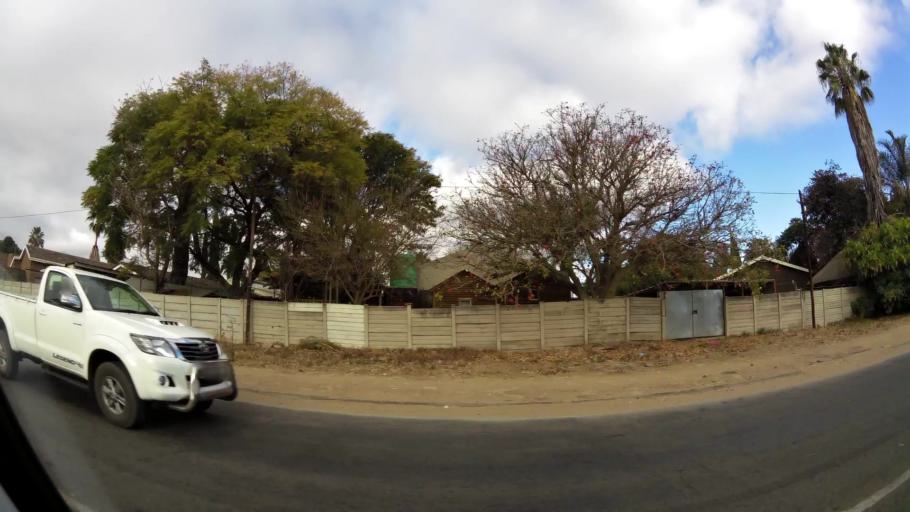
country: ZA
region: Limpopo
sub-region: Capricorn District Municipality
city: Polokwane
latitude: -23.9176
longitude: 29.4453
